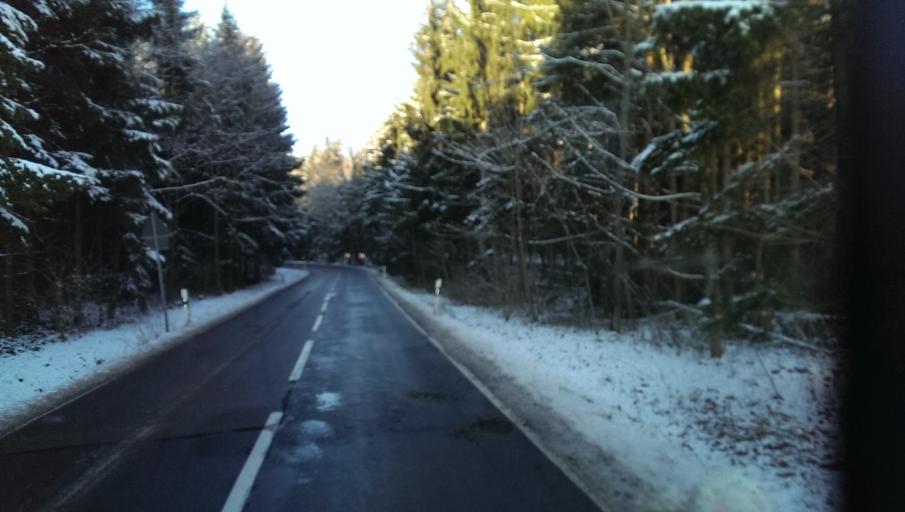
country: DE
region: Saxony
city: Dippoldiswalde
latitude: 50.8953
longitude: 13.6256
